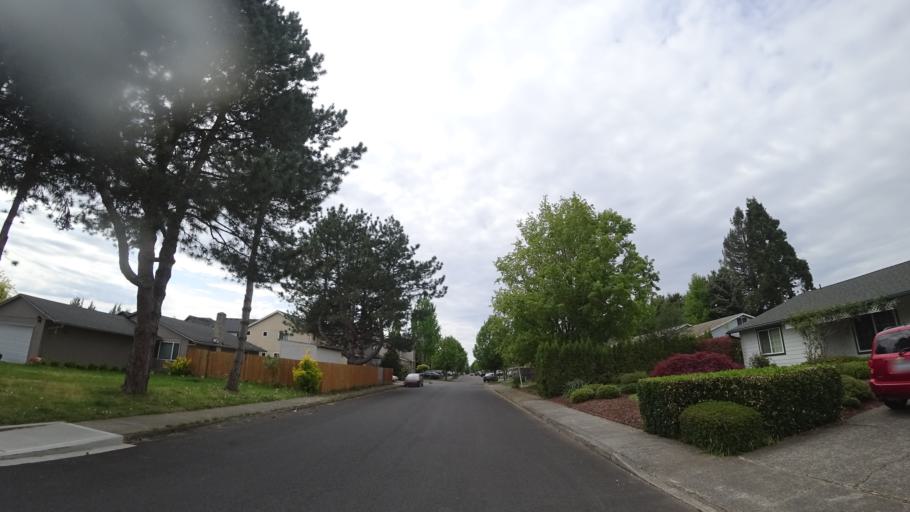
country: US
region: Oregon
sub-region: Washington County
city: Hillsboro
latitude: 45.4944
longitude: -122.9634
